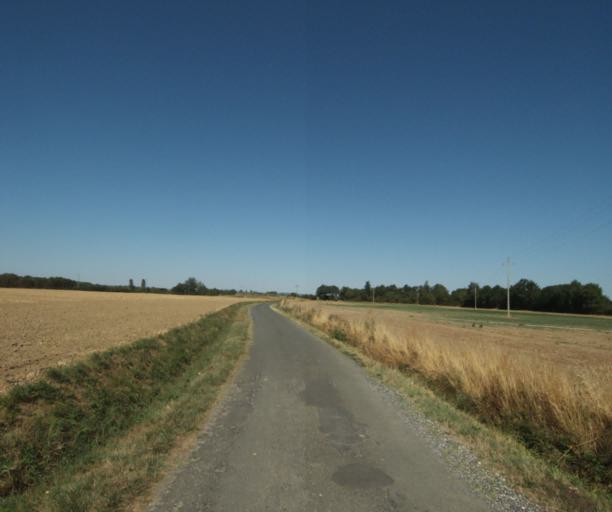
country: FR
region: Midi-Pyrenees
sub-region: Departement de la Haute-Garonne
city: Revel
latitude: 43.4562
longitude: 2.0363
